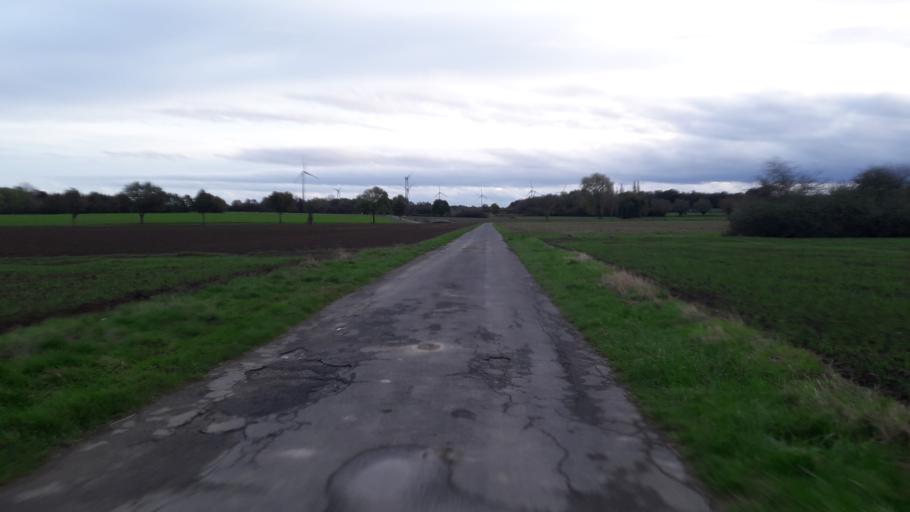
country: DE
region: North Rhine-Westphalia
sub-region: Regierungsbezirk Detmold
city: Salzkotten
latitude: 51.7322
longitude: 8.6457
